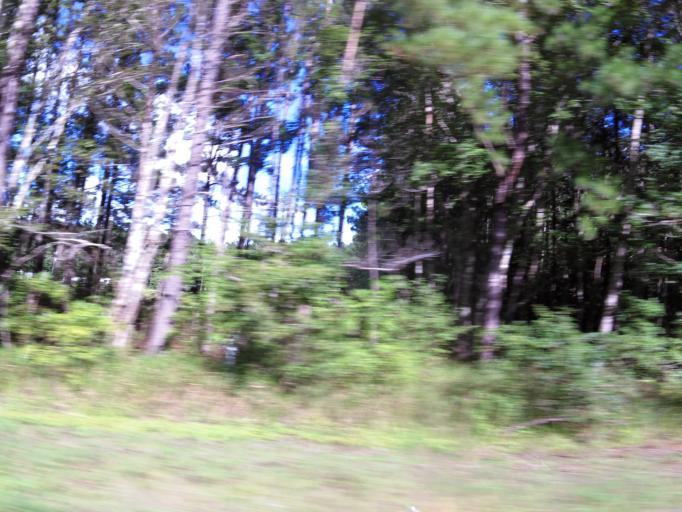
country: US
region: Georgia
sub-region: Camden County
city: Woodbine
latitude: 31.0697
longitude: -81.7279
